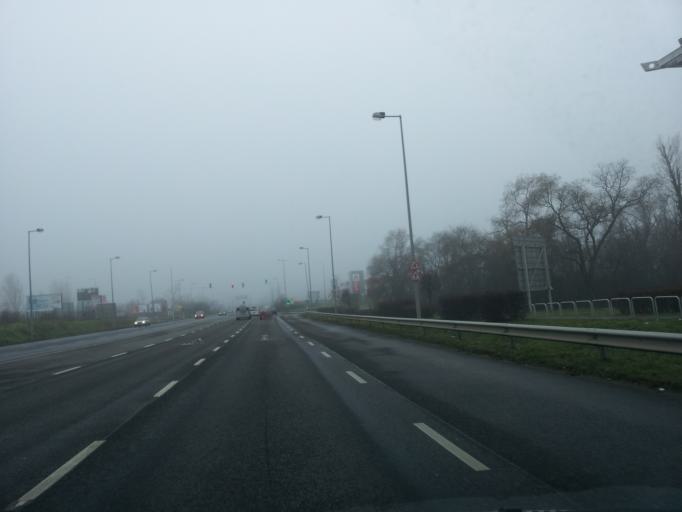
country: HU
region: Budapest
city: Budapest XXII. keruelet
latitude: 47.4344
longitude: 19.0425
